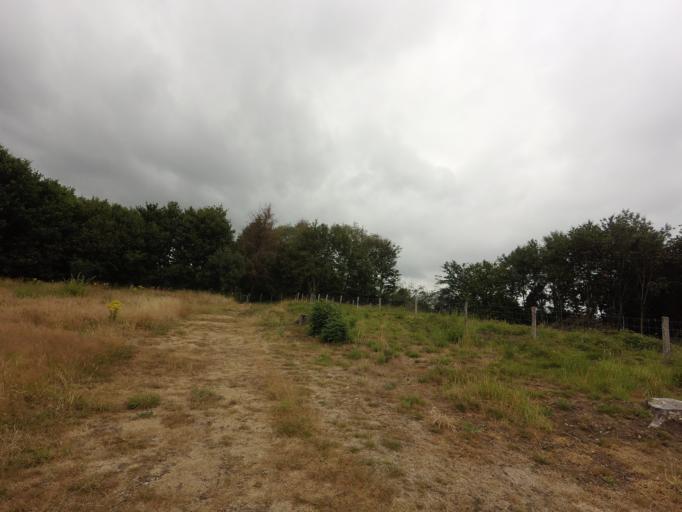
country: NL
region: Limburg
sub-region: Valkenburg aan de Geul
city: Berg
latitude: 50.8217
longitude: 5.7773
